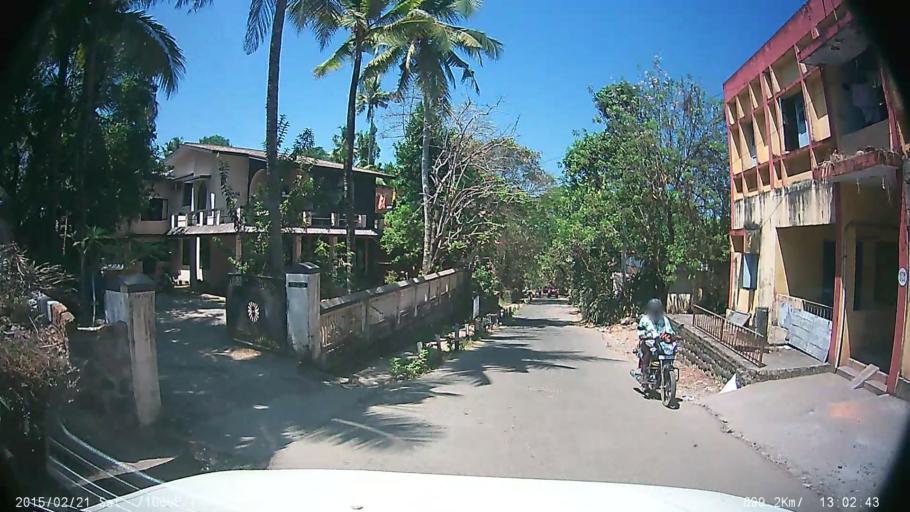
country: IN
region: Kerala
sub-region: Kottayam
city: Kottayam
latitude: 9.5913
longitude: 76.5357
